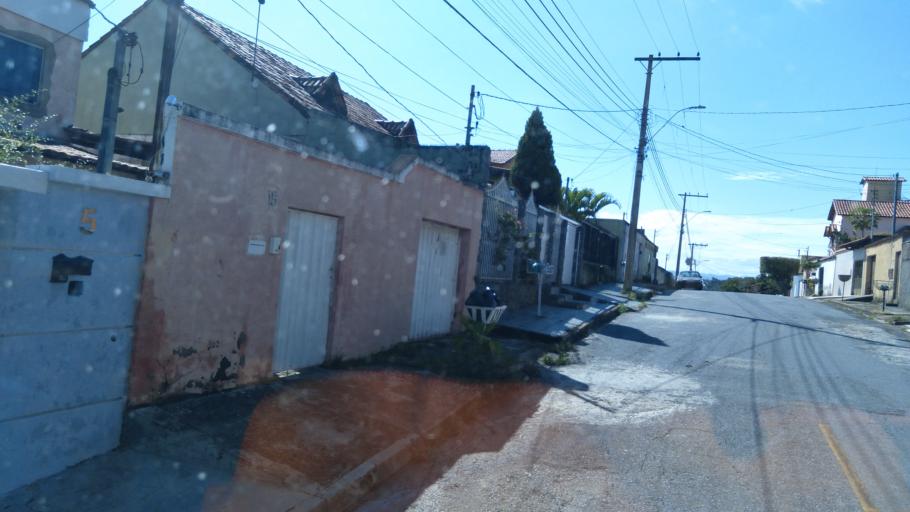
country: BR
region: Minas Gerais
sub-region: Santa Luzia
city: Santa Luzia
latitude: -19.8257
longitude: -43.9006
